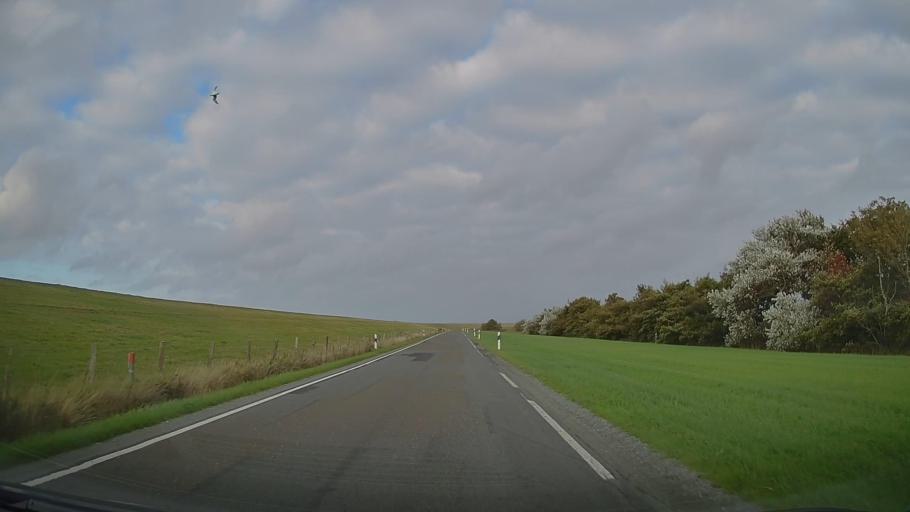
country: DE
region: Schleswig-Holstein
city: Uelvesbull
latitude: 54.4062
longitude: 8.8775
